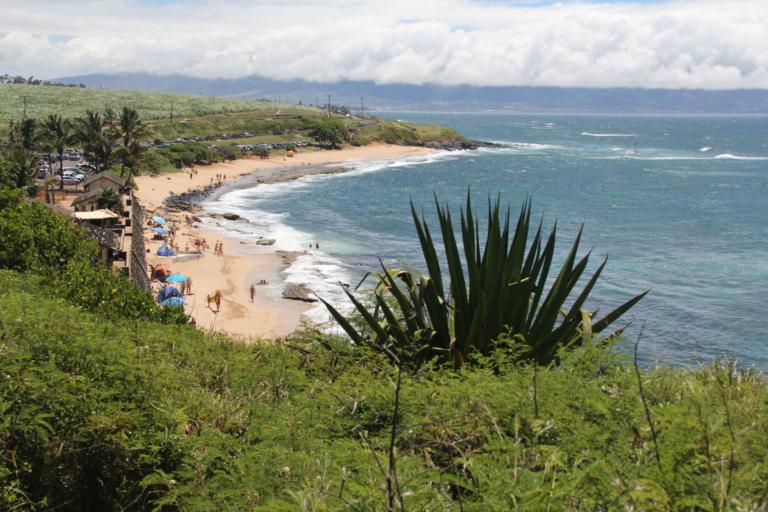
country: US
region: Hawaii
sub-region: Maui County
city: Paia
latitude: 20.9346
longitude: -156.3555
